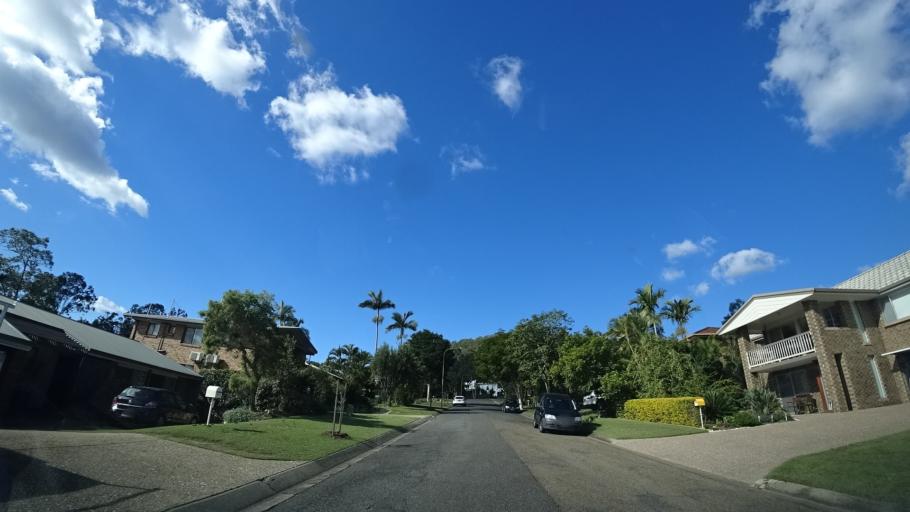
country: AU
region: Queensland
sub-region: Brisbane
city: Taringa
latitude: -27.4518
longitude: 152.9571
